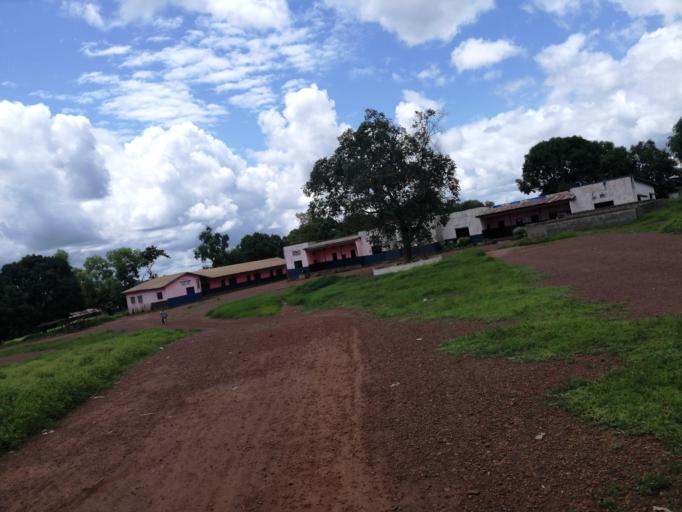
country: SL
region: Northern Province
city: Port Loko
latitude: 8.7685
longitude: -12.7812
